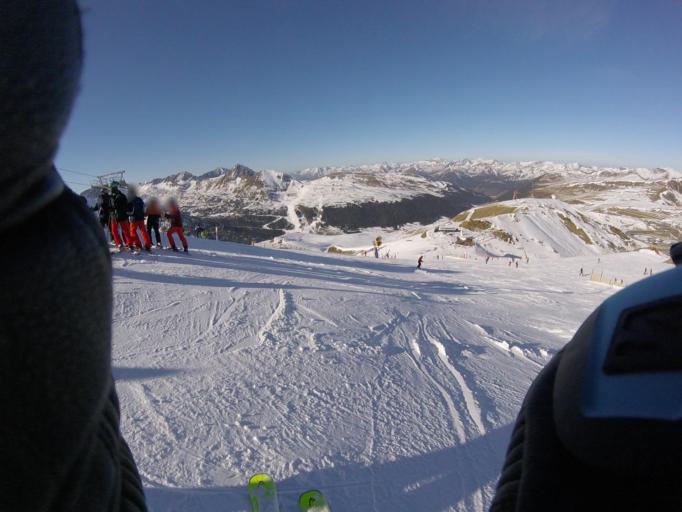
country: AD
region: Encamp
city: Pas de la Casa
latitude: 42.5258
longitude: 1.7238
